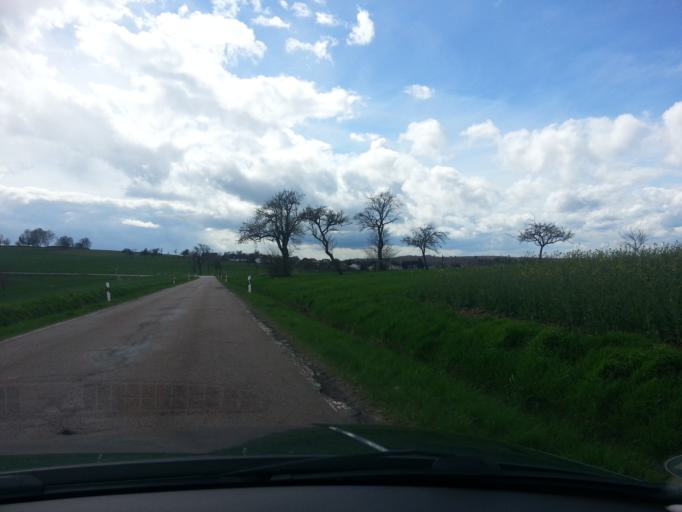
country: DE
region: Rheinland-Pfalz
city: Schmitshausen
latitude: 49.2866
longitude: 7.5222
